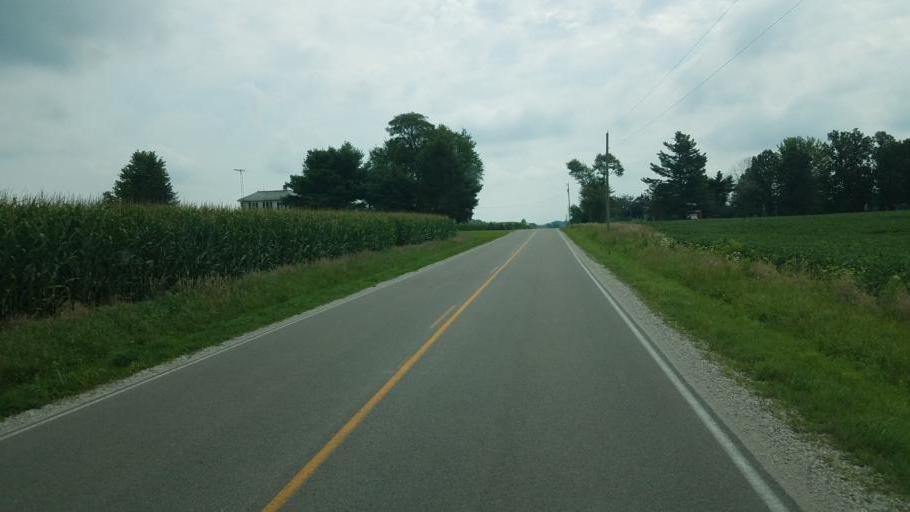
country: US
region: Ohio
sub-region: Crawford County
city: Bucyrus
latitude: 40.7183
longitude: -82.9501
